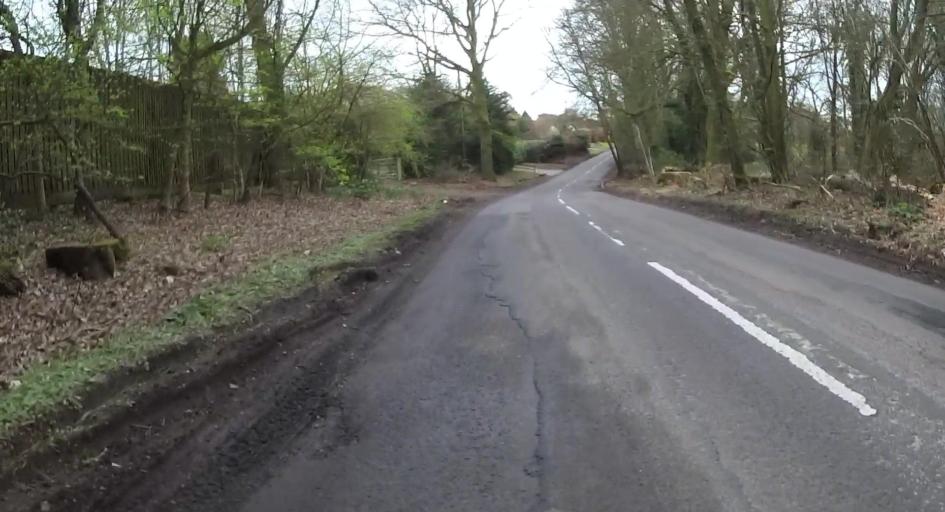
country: GB
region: England
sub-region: Hampshire
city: Alton
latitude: 51.1766
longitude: -0.9821
